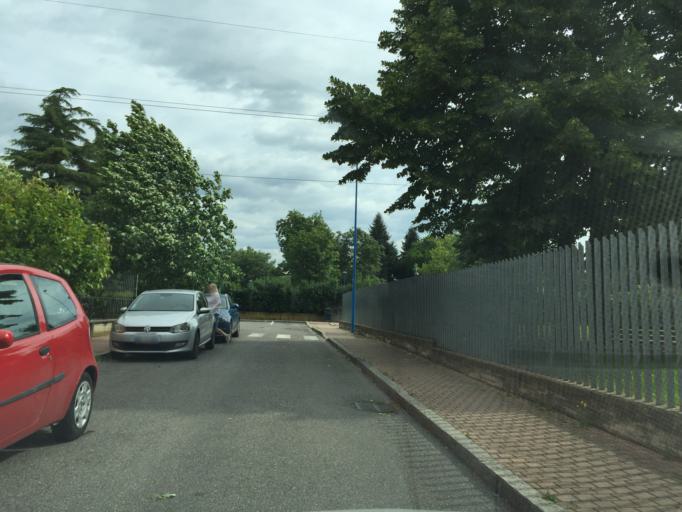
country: IT
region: Lombardy
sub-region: Provincia di Brescia
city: Folzano
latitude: 45.5135
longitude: 10.1910
